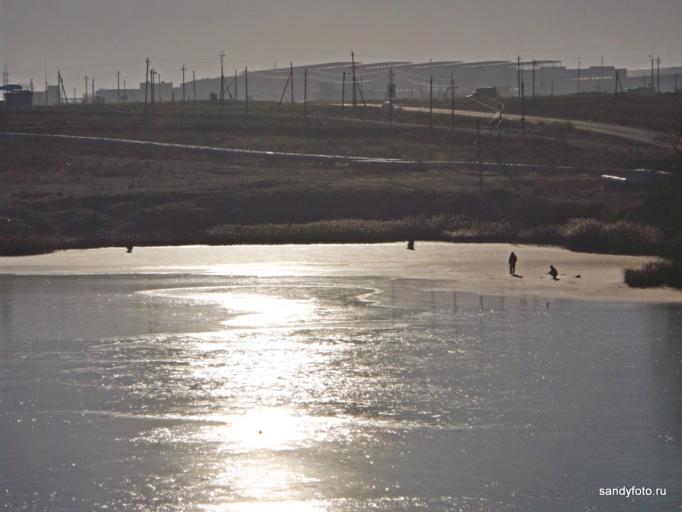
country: RU
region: Chelyabinsk
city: Troitsk
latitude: 54.0772
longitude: 61.5564
